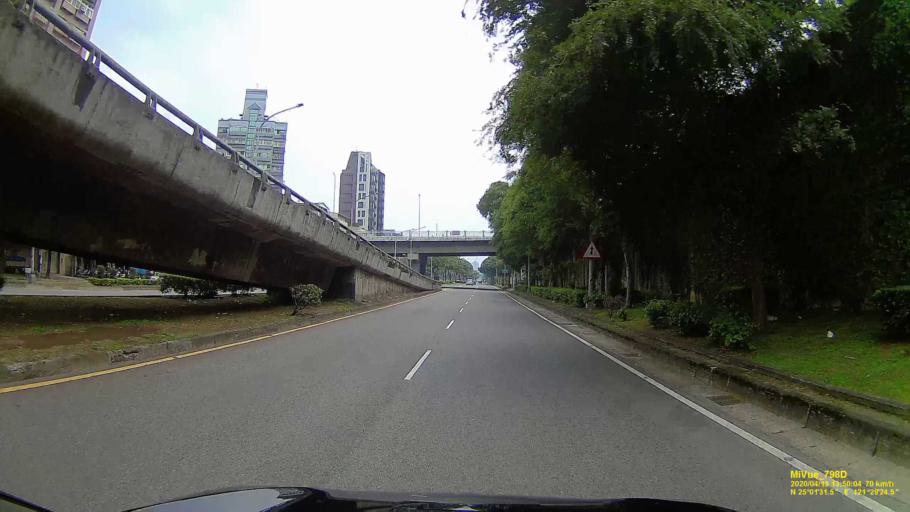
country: TW
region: Taipei
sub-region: Taipei
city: Banqiao
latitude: 25.0250
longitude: 121.4903
